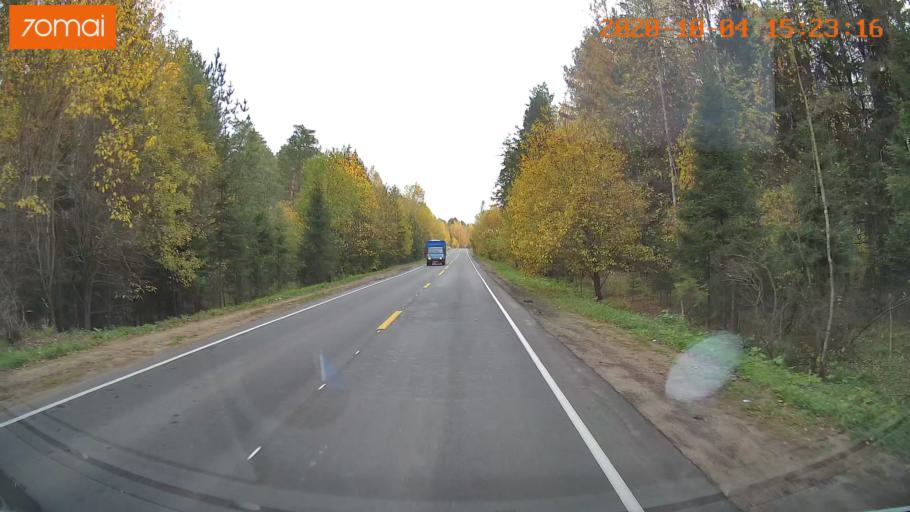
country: RU
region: Ivanovo
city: Bogorodskoye
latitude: 57.0752
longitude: 40.9472
